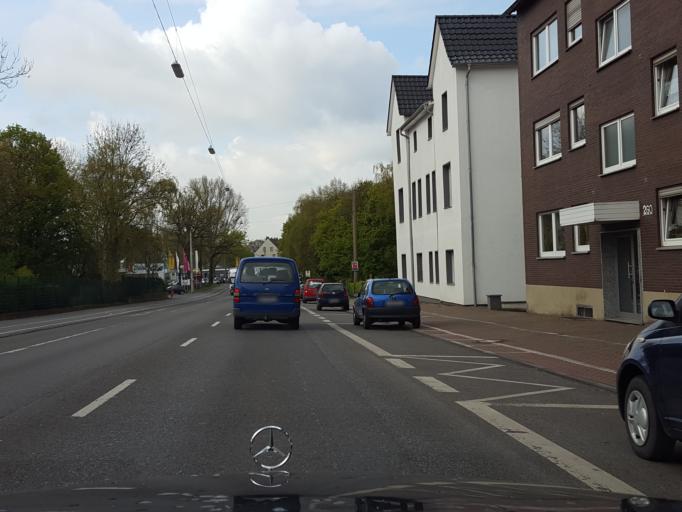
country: DE
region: North Rhine-Westphalia
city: Datteln
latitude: 51.6339
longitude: 7.3312
